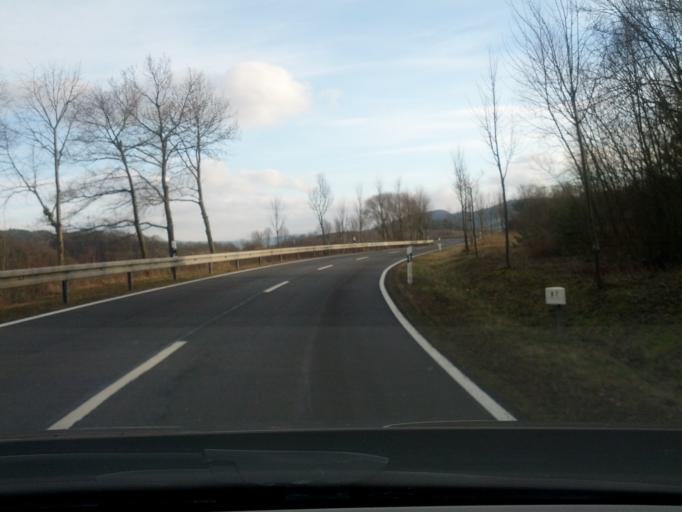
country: DE
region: Thuringia
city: Ifta
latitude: 51.0745
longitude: 10.1555
